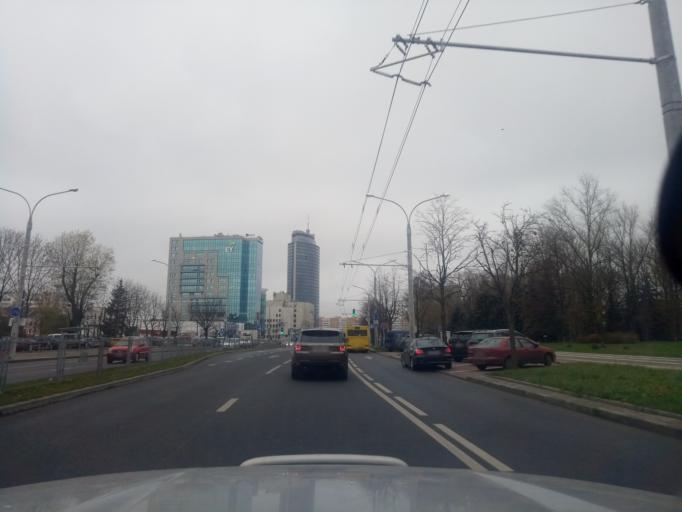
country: BY
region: Minsk
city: Minsk
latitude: 53.9020
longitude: 27.5340
